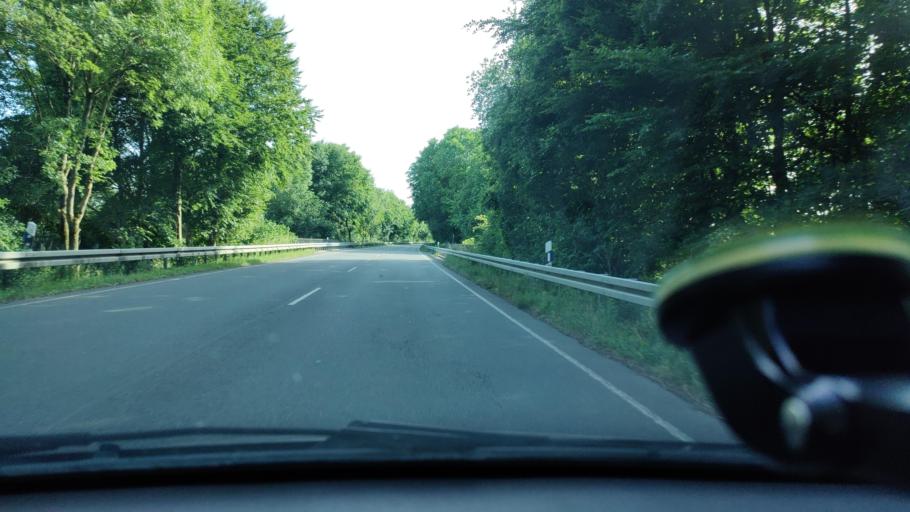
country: DE
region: North Rhine-Westphalia
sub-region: Regierungsbezirk Munster
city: Billerbeck
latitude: 52.0187
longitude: 7.2255
